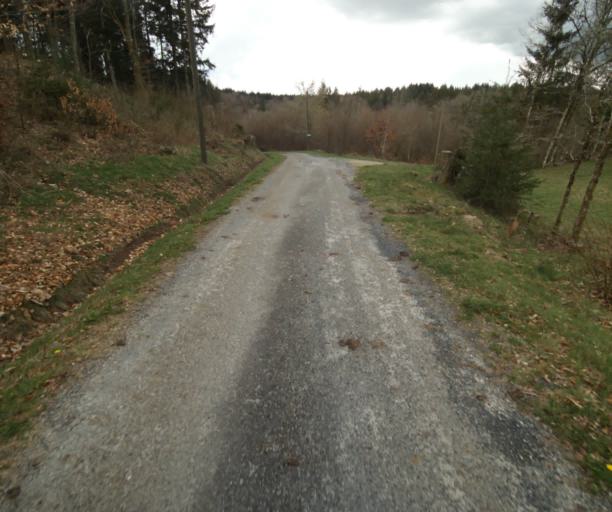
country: FR
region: Limousin
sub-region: Departement de la Correze
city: Correze
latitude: 45.2665
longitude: 1.9574
